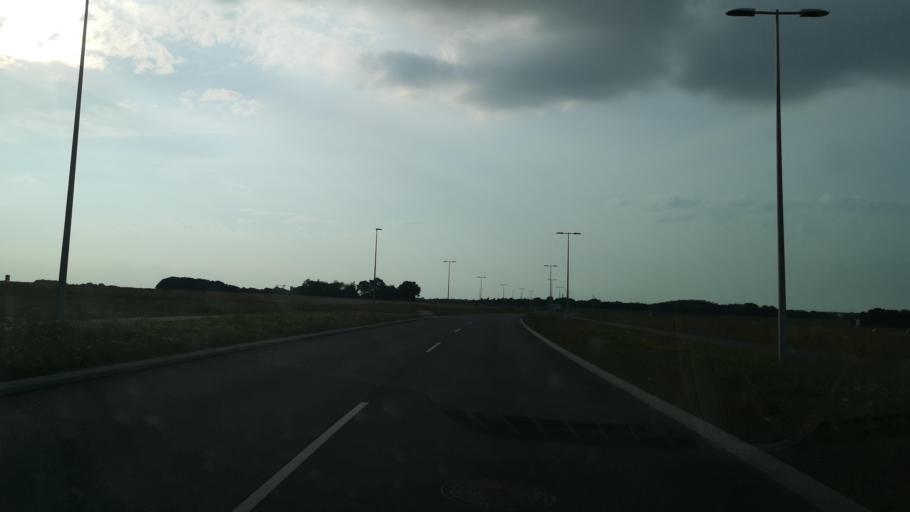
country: DK
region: Central Jutland
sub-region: Herning Kommune
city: Snejbjerg
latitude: 56.1214
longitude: 8.9192
